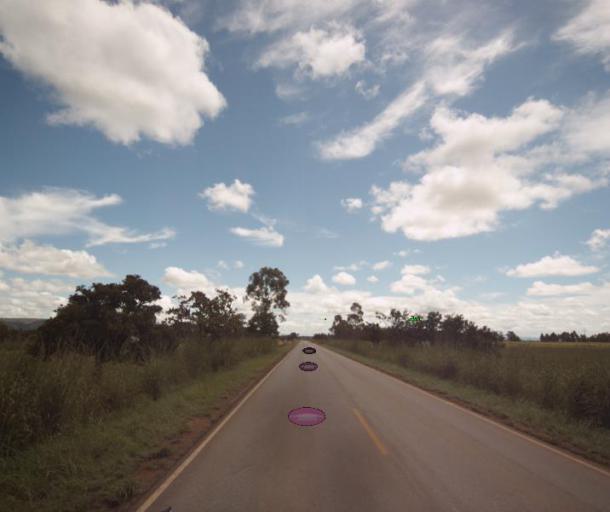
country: BR
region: Goias
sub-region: Padre Bernardo
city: Padre Bernardo
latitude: -15.3854
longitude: -48.2081
